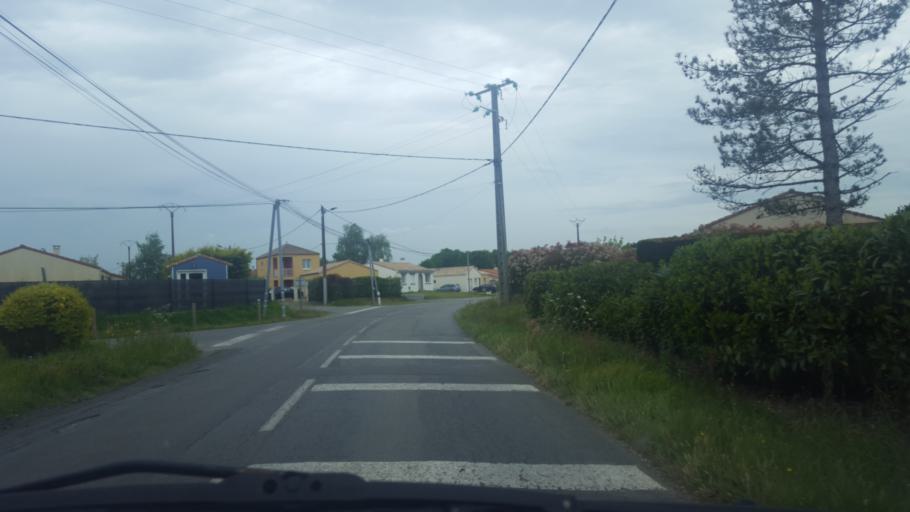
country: FR
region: Pays de la Loire
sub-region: Departement de la Loire-Atlantique
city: La Limouziniere
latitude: 47.0199
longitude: -1.5597
